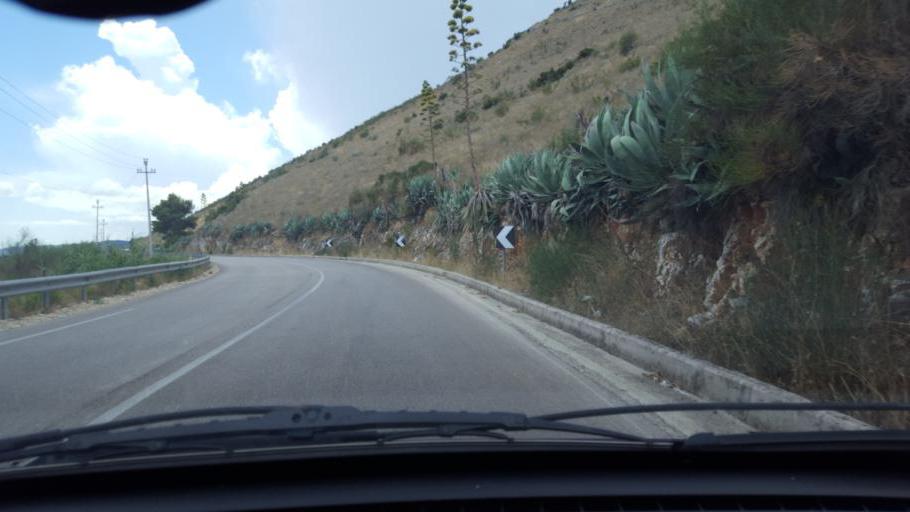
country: AL
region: Vlore
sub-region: Rrethi i Sarandes
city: Sarande
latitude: 39.8334
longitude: 20.0228
